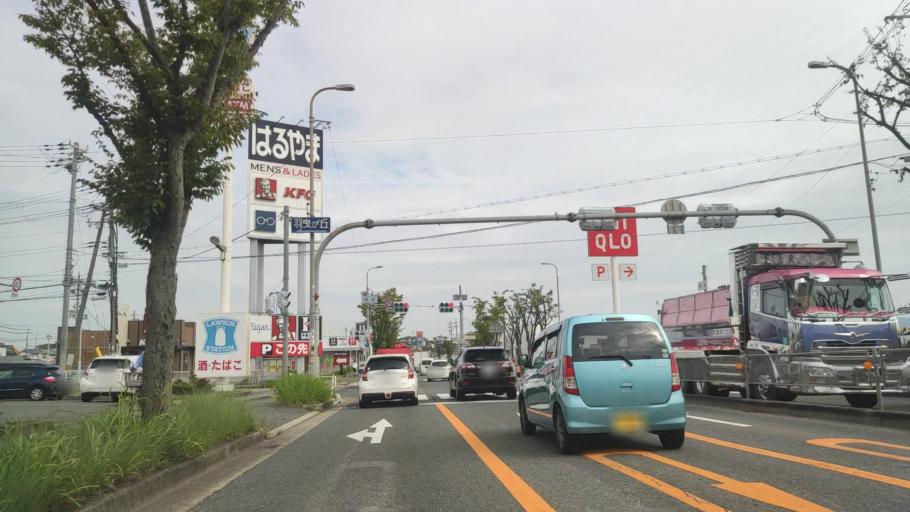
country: JP
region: Osaka
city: Tondabayashicho
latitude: 34.5411
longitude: 135.6046
